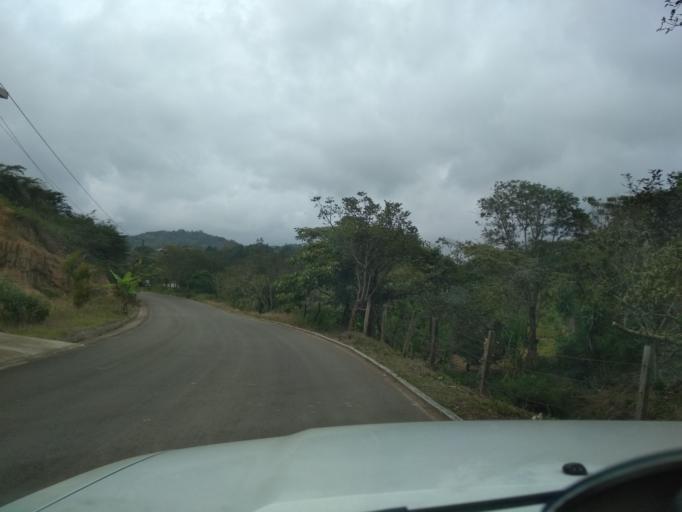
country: MX
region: Veracruz
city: El Castillo
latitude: 19.5480
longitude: -96.8468
